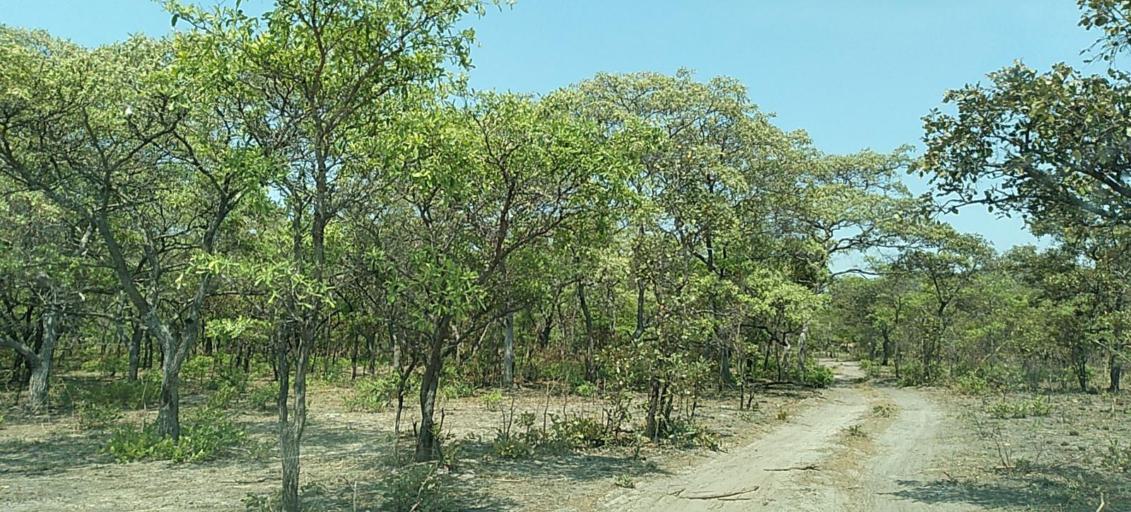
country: ZM
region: Copperbelt
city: Mpongwe
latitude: -13.8436
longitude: 28.0594
